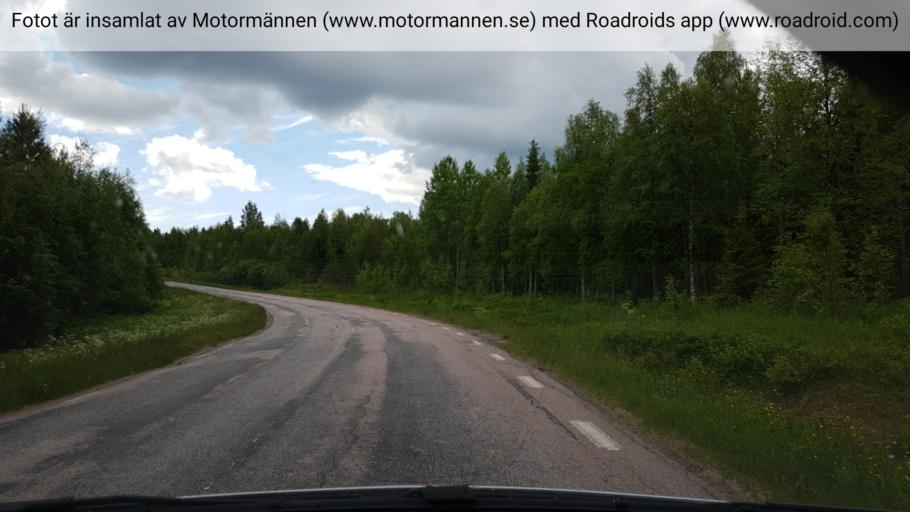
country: FI
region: Lapland
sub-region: Torniolaakso
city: Ylitornio
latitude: 66.2023
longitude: 23.7028
